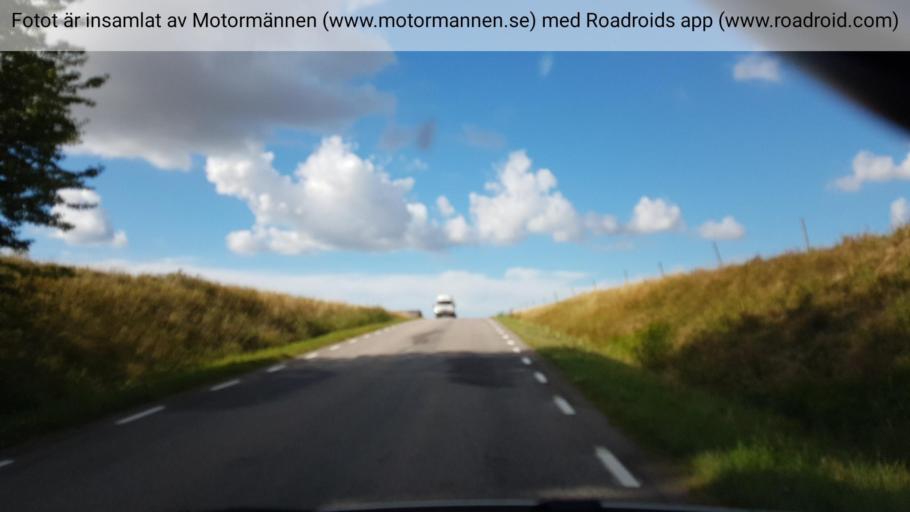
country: SE
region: Vaestra Goetaland
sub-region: Lidkopings Kommun
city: Vinninga
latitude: 58.4445
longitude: 13.3392
